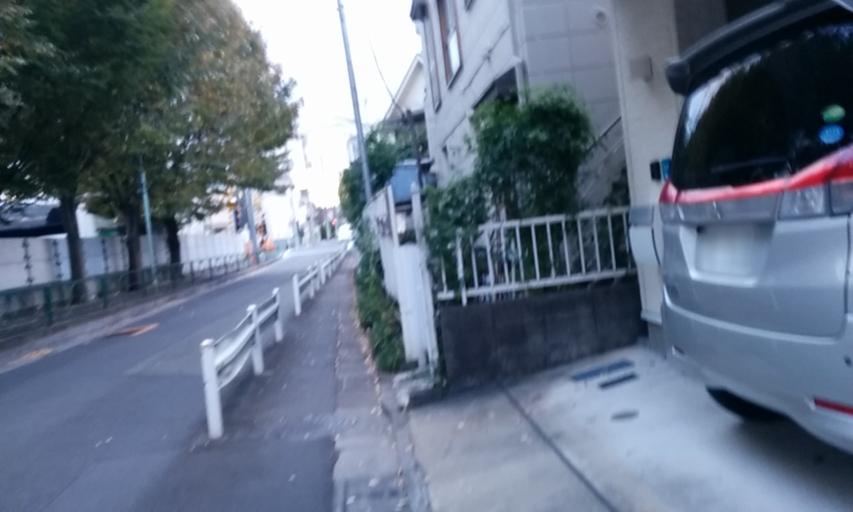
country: JP
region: Tokyo
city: Tokyo
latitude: 35.6777
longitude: 139.6404
